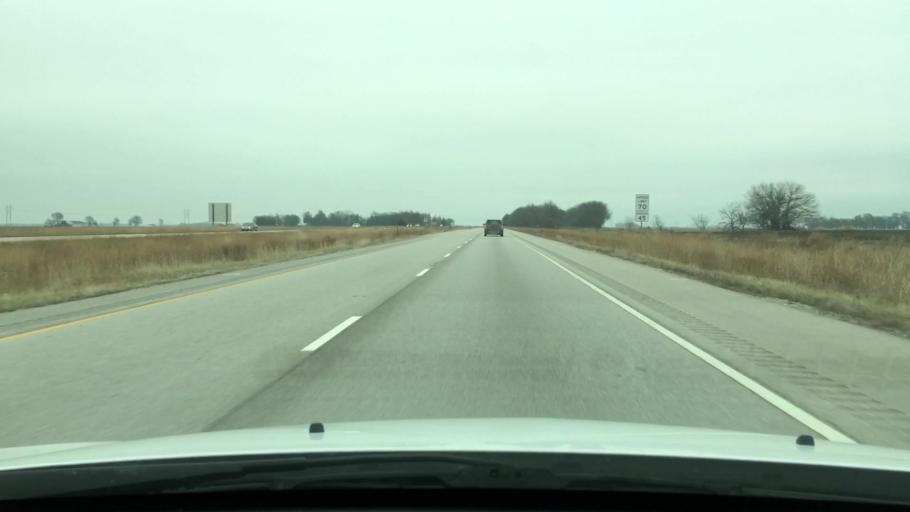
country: US
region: Illinois
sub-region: Sangamon County
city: New Berlin
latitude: 39.7368
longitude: -90.0298
